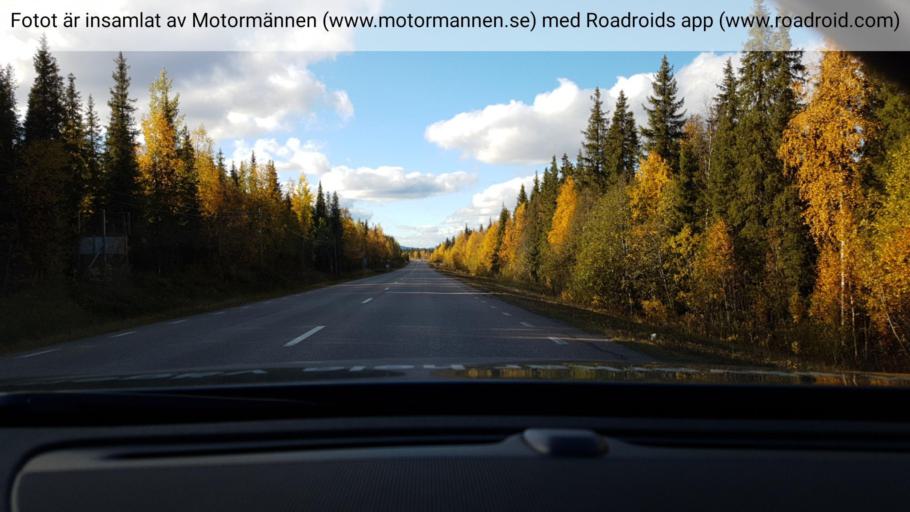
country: SE
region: Norrbotten
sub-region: Gallivare Kommun
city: Gaellivare
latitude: 67.1255
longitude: 20.6428
